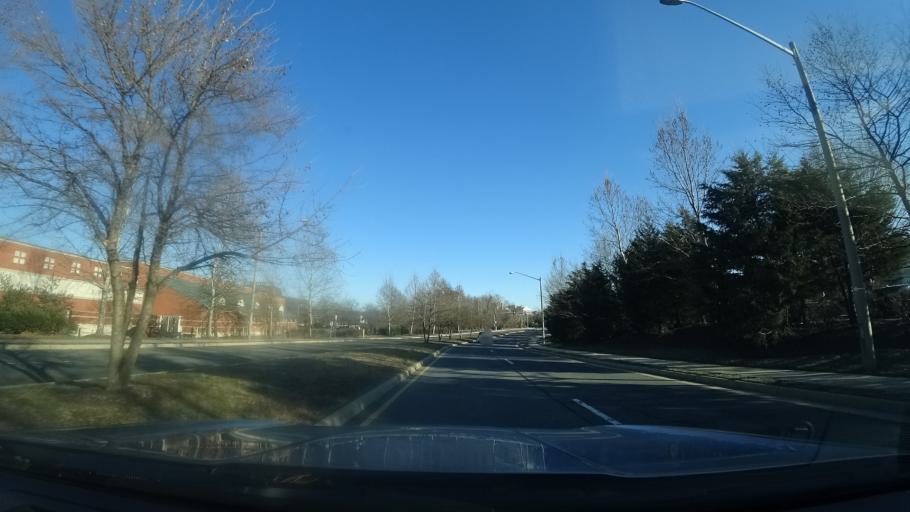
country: US
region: Virginia
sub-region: Fairfax County
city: Herndon
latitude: 38.9664
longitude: -77.3775
